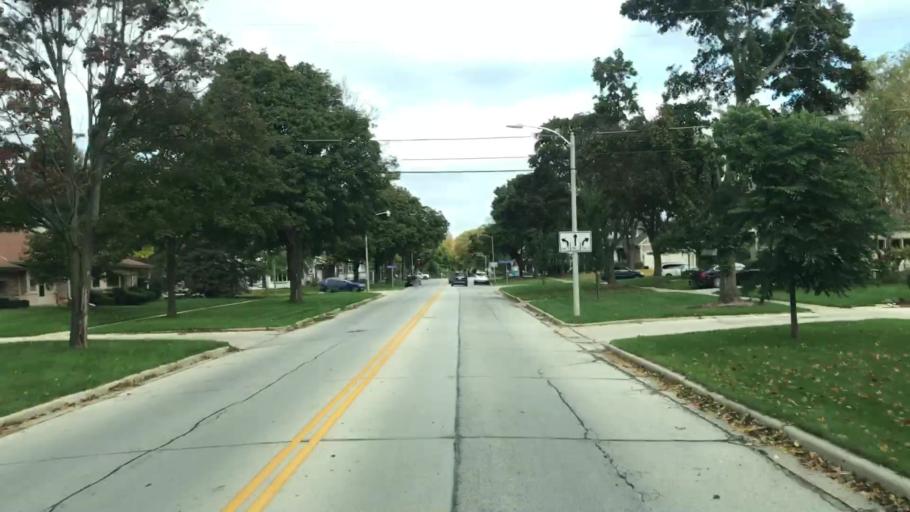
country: US
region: Wisconsin
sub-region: Milwaukee County
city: Wauwatosa
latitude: 43.0586
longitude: -88.0274
